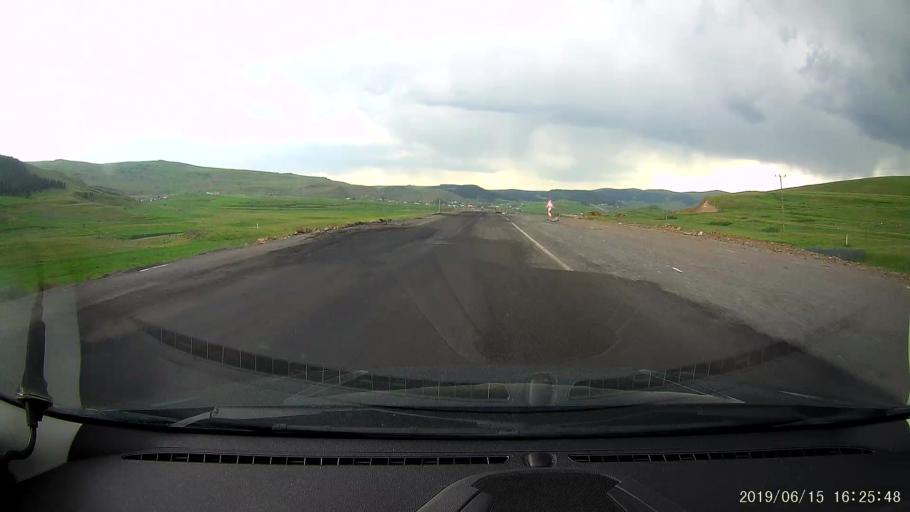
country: TR
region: Ardahan
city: Hanak
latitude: 41.1490
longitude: 42.8665
